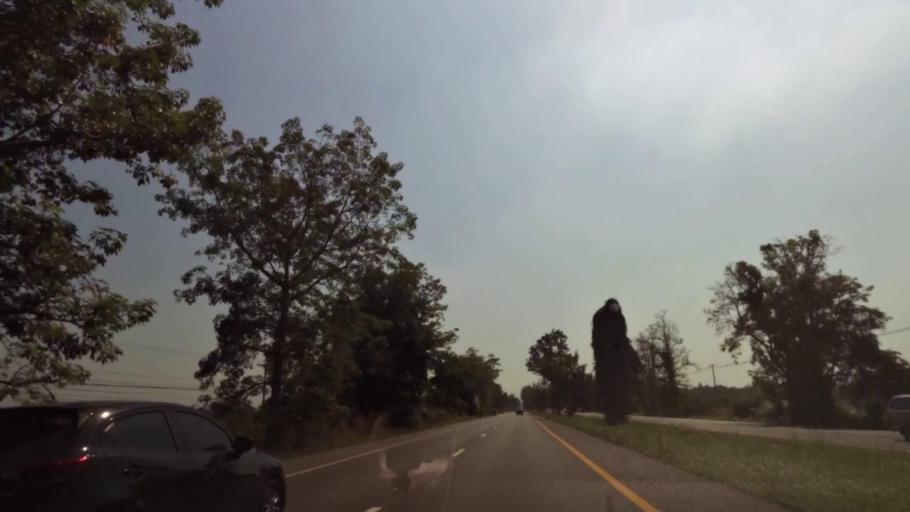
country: TH
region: Nakhon Sawan
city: Banphot Phisai
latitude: 16.0065
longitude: 100.1156
